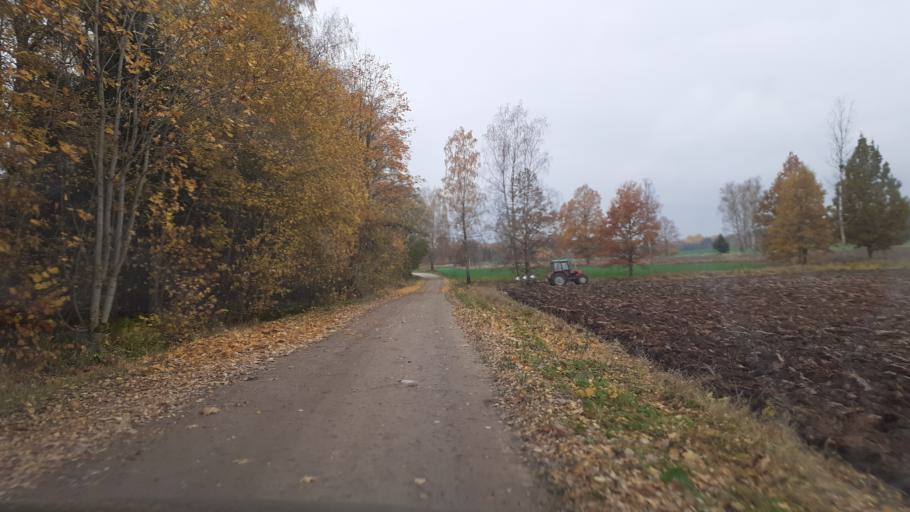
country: LV
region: Saldus Rajons
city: Saldus
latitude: 56.8772
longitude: 22.2967
